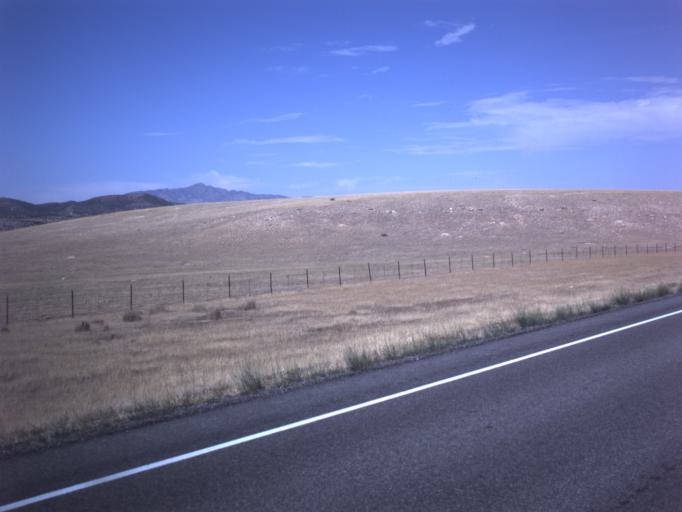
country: US
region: Utah
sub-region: Sanpete County
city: Gunnison
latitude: 39.3325
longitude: -111.9159
